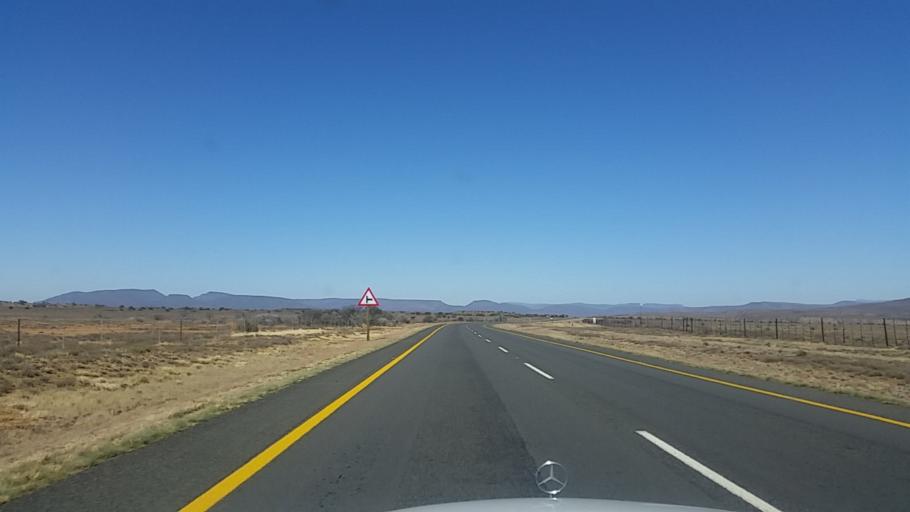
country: ZA
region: Eastern Cape
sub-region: Cacadu District Municipality
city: Graaff-Reinet
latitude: -32.1307
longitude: 24.5875
